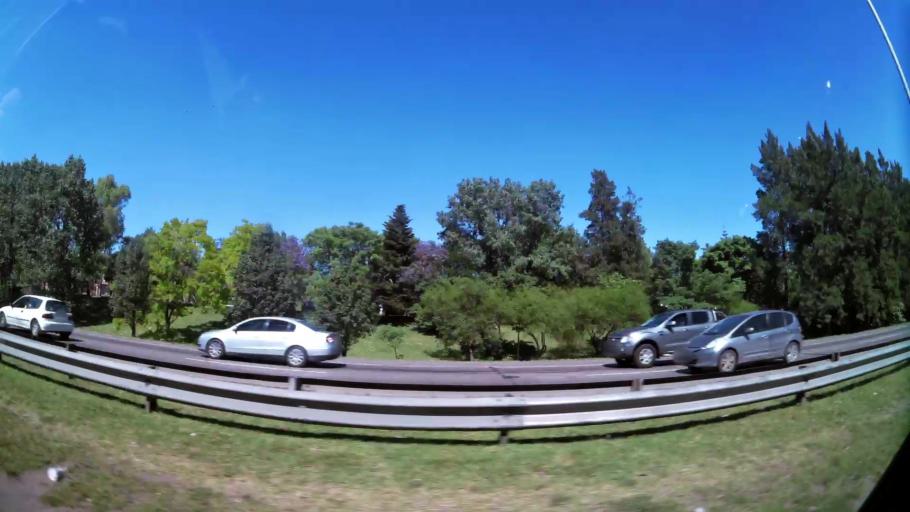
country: AR
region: Buenos Aires
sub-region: Partido de Tigre
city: Tigre
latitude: -34.4754
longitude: -58.5645
